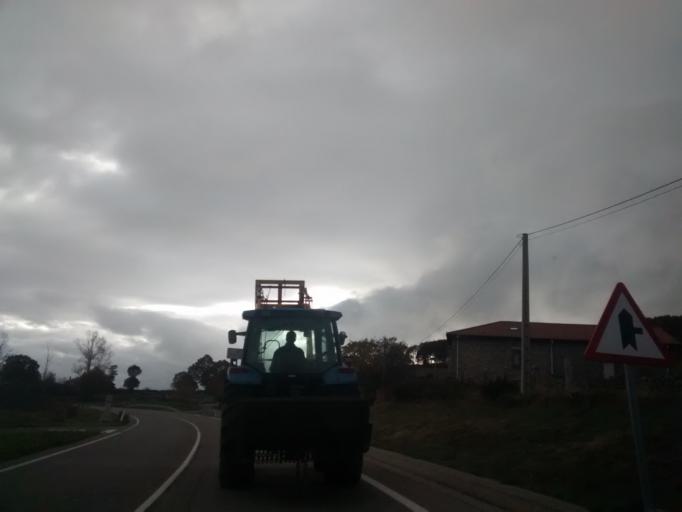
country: ES
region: Castille and Leon
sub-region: Provincia de Burgos
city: Arija
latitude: 43.0347
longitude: -3.9402
